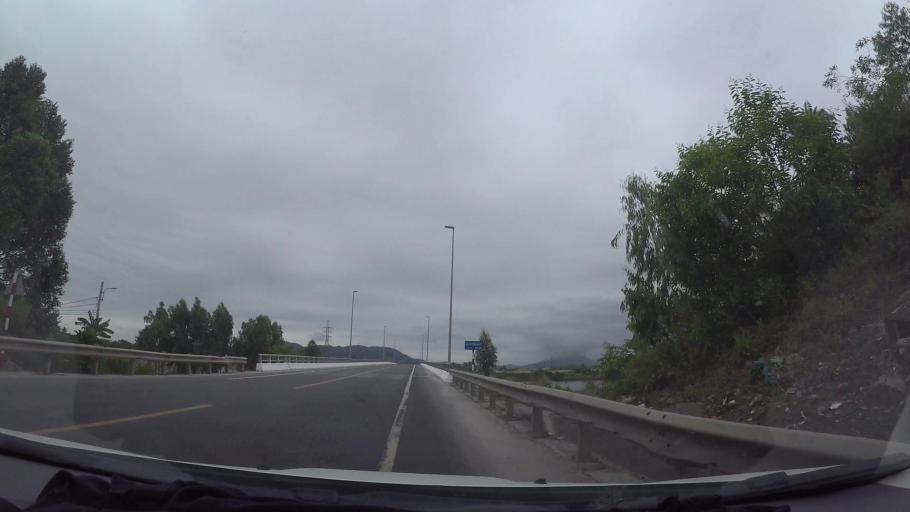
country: VN
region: Da Nang
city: Lien Chieu
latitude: 16.1164
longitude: 108.1042
